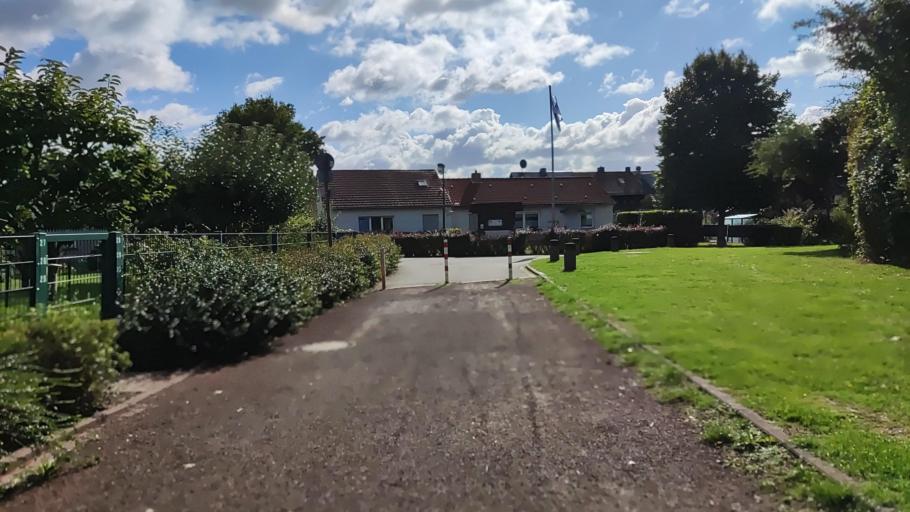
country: DE
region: North Rhine-Westphalia
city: Bochum-Hordel
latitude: 51.5218
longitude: 7.1749
